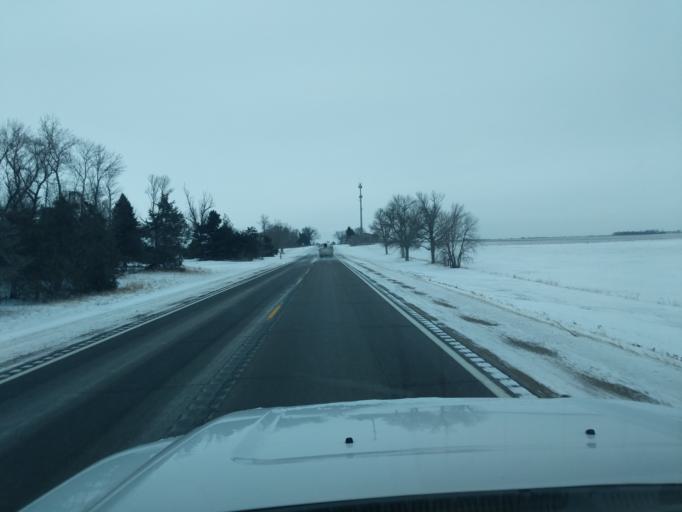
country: US
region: Minnesota
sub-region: Redwood County
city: Redwood Falls
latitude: 44.6027
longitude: -94.9945
